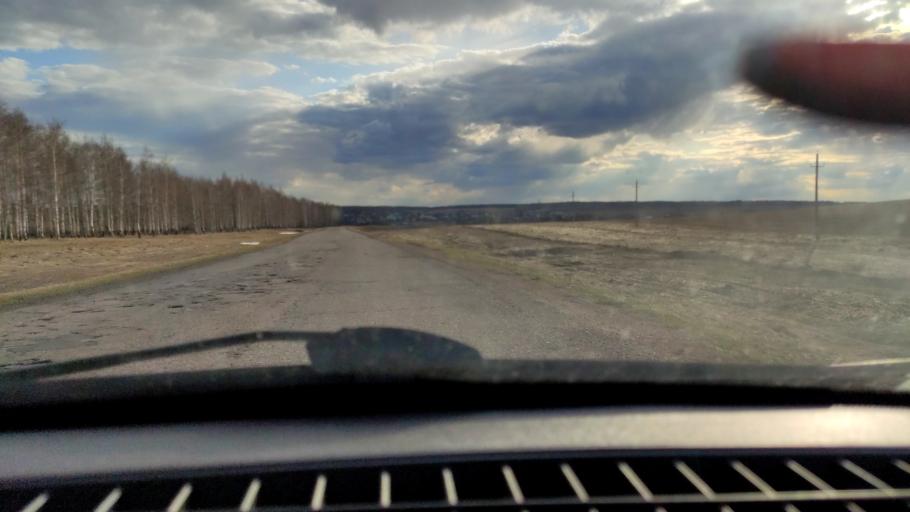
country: RU
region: Bashkortostan
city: Karmaskaly
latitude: 54.3437
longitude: 56.0206
